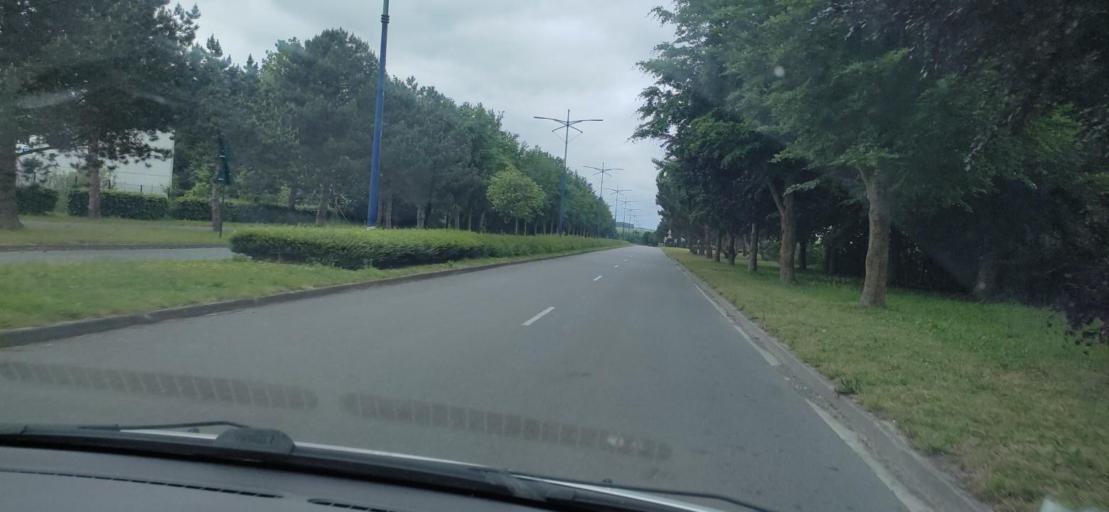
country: FR
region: Nord-Pas-de-Calais
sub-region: Departement du Pas-de-Calais
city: Feuchy
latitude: 50.2738
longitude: 2.8538
